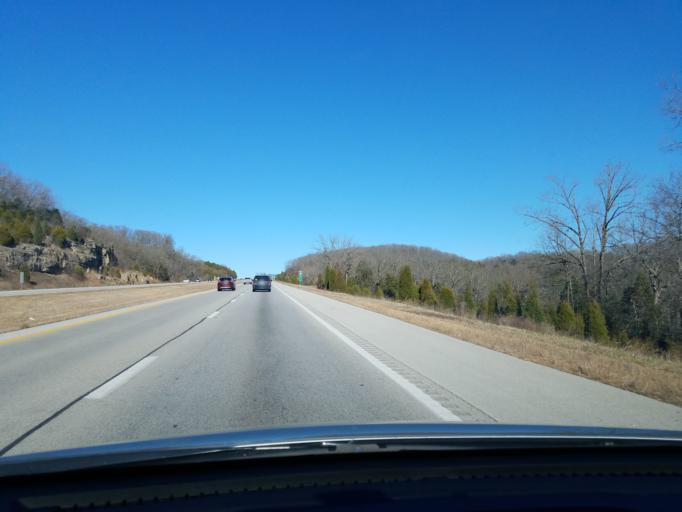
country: US
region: Missouri
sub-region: Taney County
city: Merriam Woods
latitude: 36.7837
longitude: -93.2246
